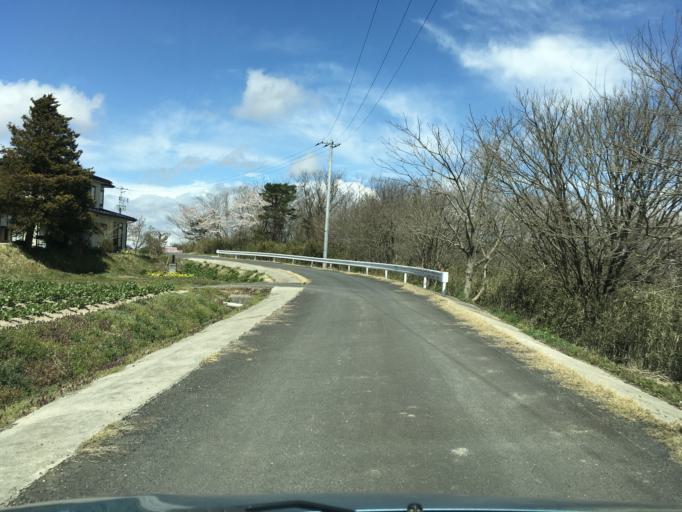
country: JP
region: Miyagi
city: Wakuya
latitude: 38.6811
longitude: 141.1231
